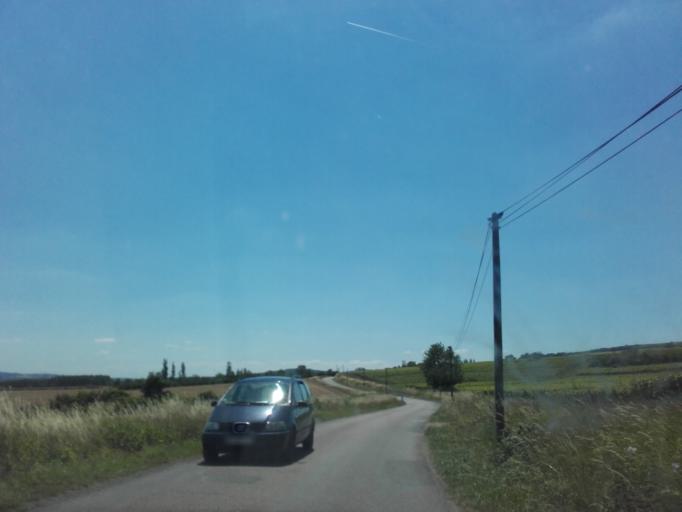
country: FR
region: Bourgogne
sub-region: Departement de Saone-et-Loire
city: Saint-Leger-sur-Dheune
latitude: 46.8916
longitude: 4.6589
